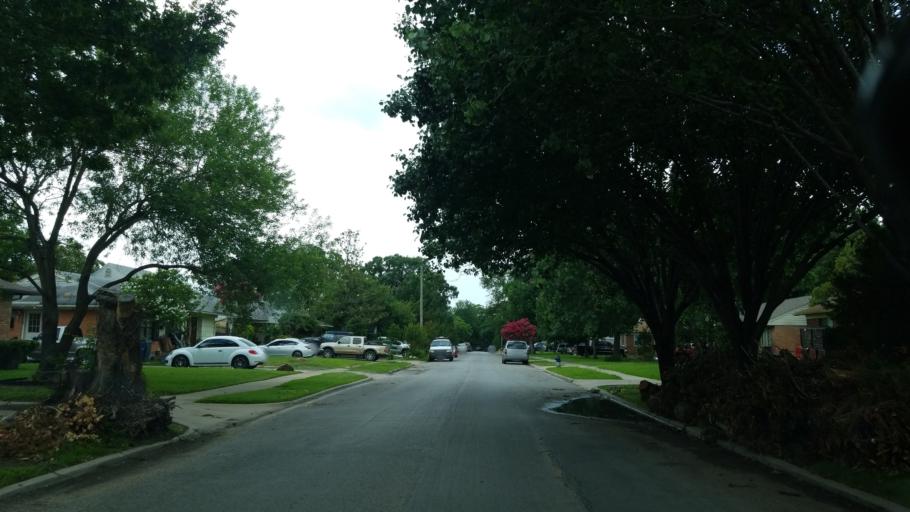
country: US
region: Texas
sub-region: Dallas County
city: Farmers Branch
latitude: 32.8799
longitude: -96.8596
